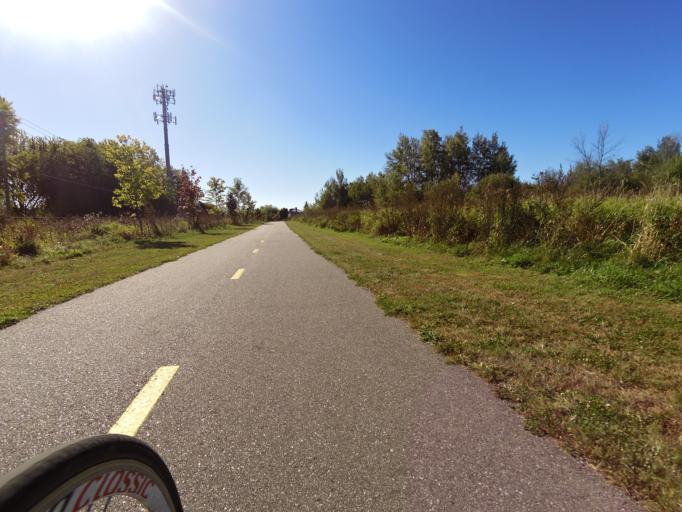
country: CA
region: Quebec
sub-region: Outaouais
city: Gatineau
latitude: 45.4755
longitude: -75.6731
